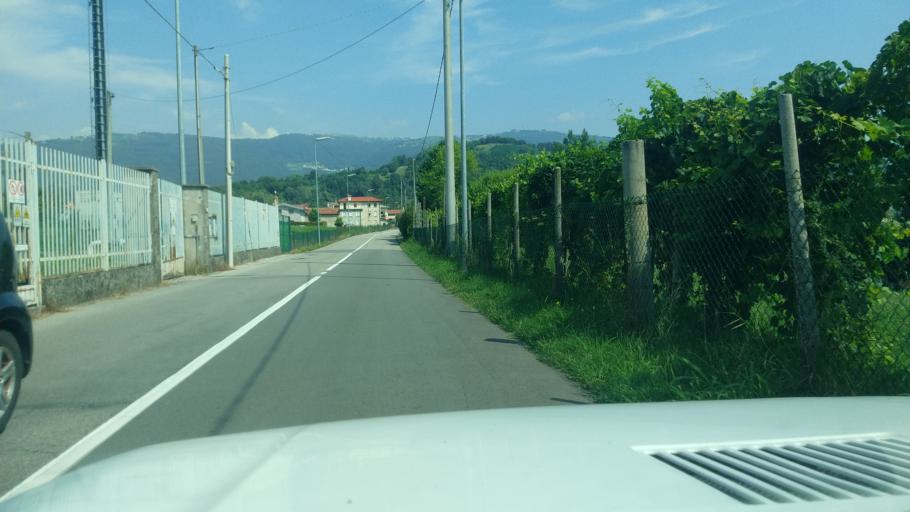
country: IT
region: Veneto
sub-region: Provincia di Vicenza
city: Marostica
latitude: 45.7465
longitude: 11.6690
